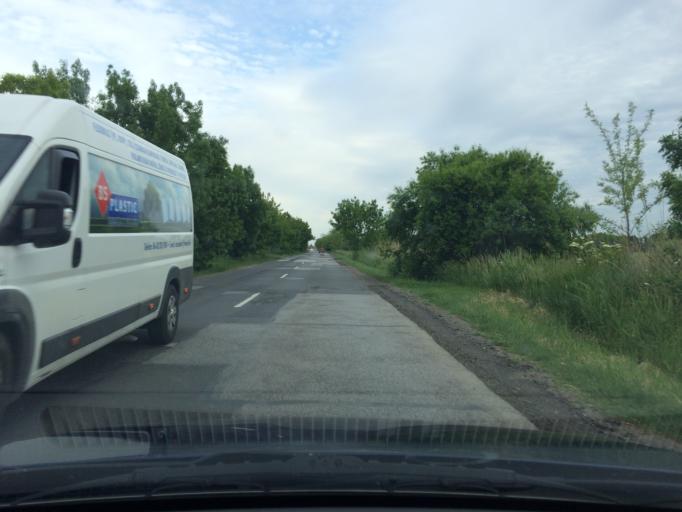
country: HU
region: Hajdu-Bihar
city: Hajdunanas
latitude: 47.8917
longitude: 21.4115
